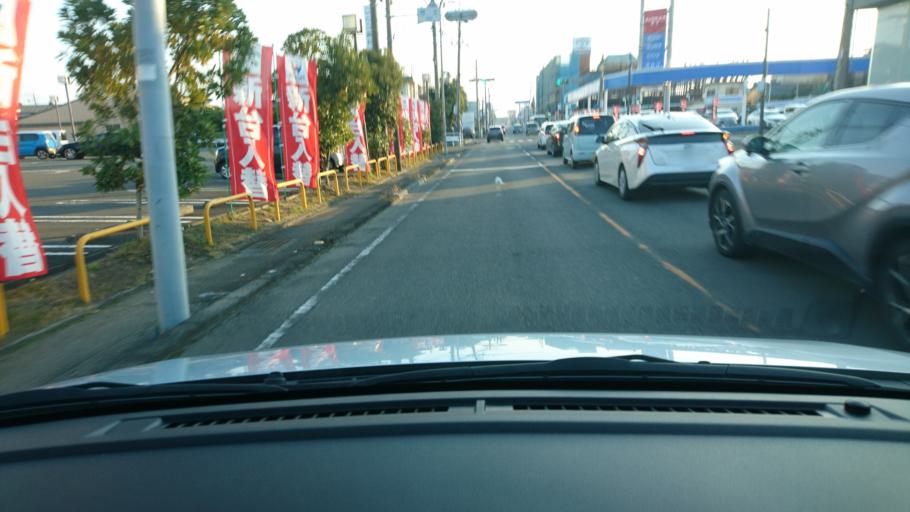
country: JP
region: Miyazaki
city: Miyazaki-shi
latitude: 31.9619
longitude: 131.4382
